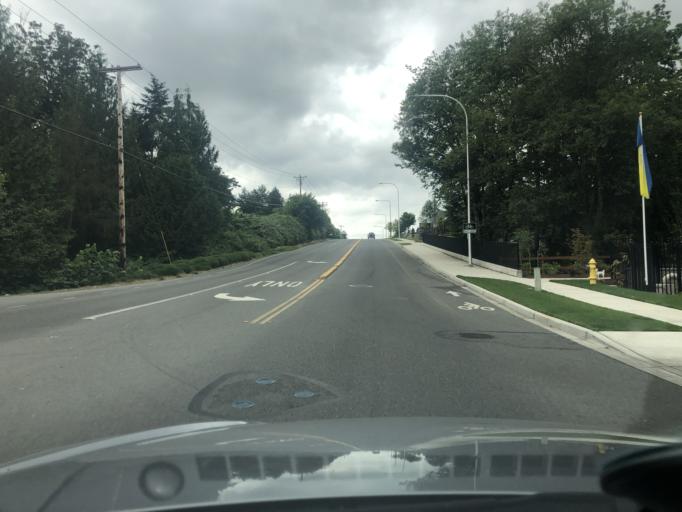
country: US
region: Washington
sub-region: King County
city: Lea Hill
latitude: 47.3225
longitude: -122.1691
